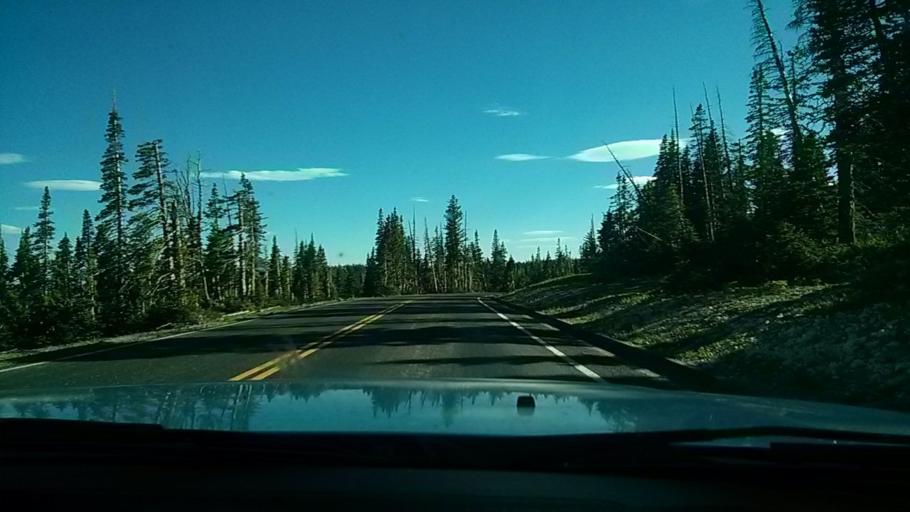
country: US
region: Utah
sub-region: Iron County
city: Parowan
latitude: 37.6147
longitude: -112.8296
